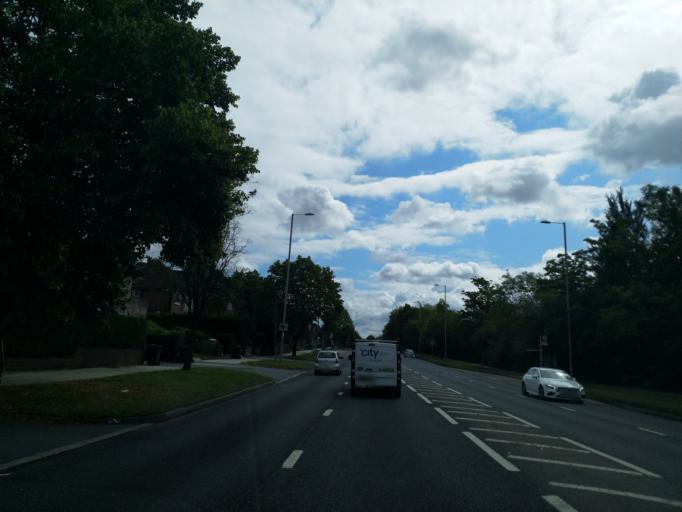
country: GB
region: England
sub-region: Greater London
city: Belsize Park
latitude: 51.5856
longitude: -0.1794
